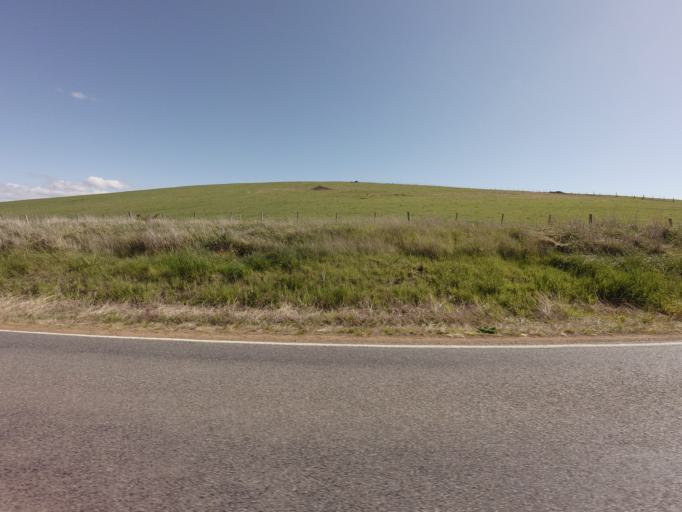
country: AU
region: Tasmania
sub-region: Derwent Valley
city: New Norfolk
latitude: -42.6464
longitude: 146.9243
